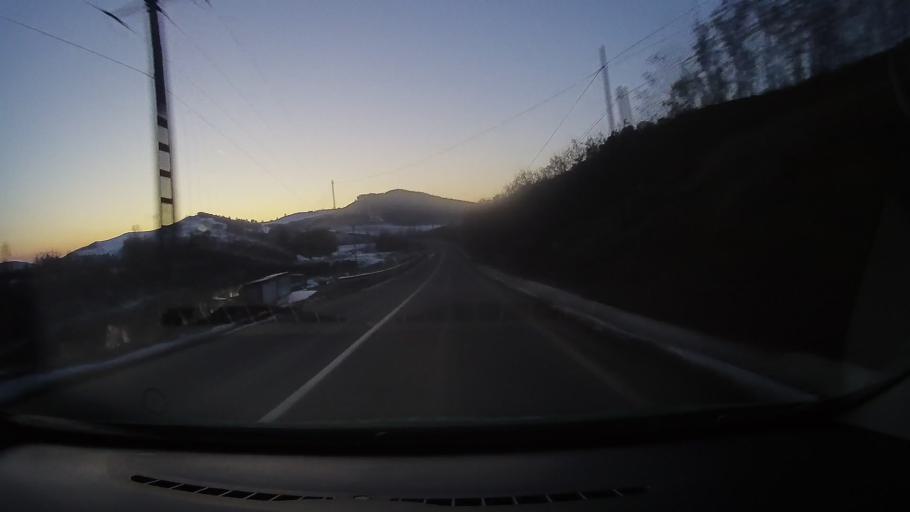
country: RO
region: Sibiu
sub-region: Comuna Alma
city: Alma
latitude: 46.2030
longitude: 24.4617
